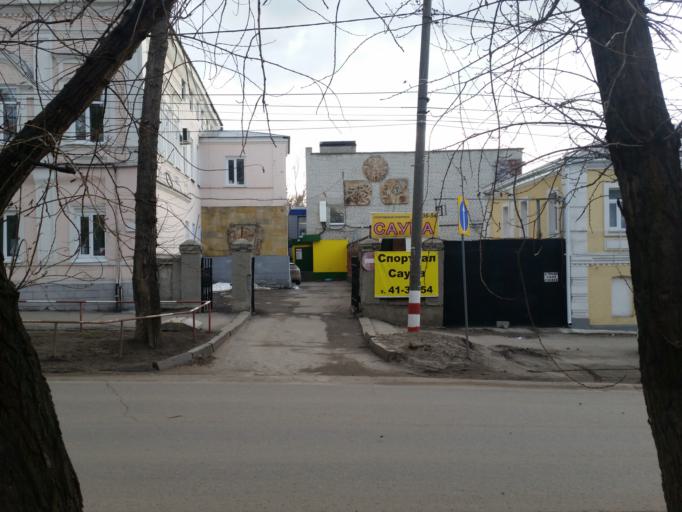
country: RU
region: Ulyanovsk
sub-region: Ulyanovskiy Rayon
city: Ulyanovsk
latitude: 54.3145
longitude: 48.3886
